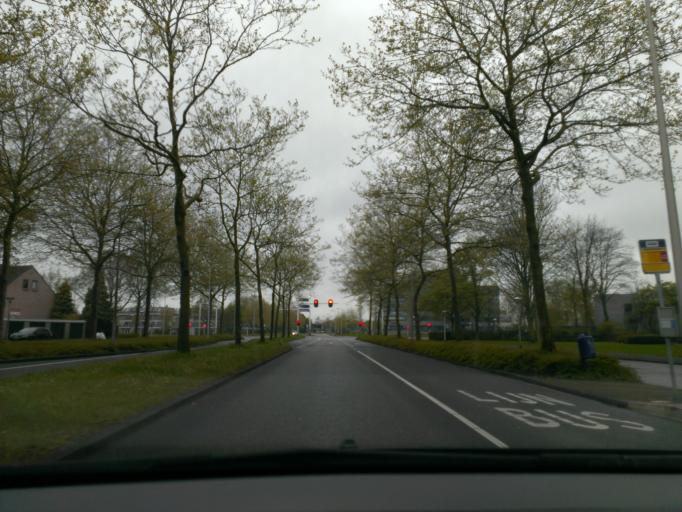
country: NL
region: Overijssel
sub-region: Gemeente Zwolle
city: Zwolle
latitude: 52.5264
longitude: 6.1030
